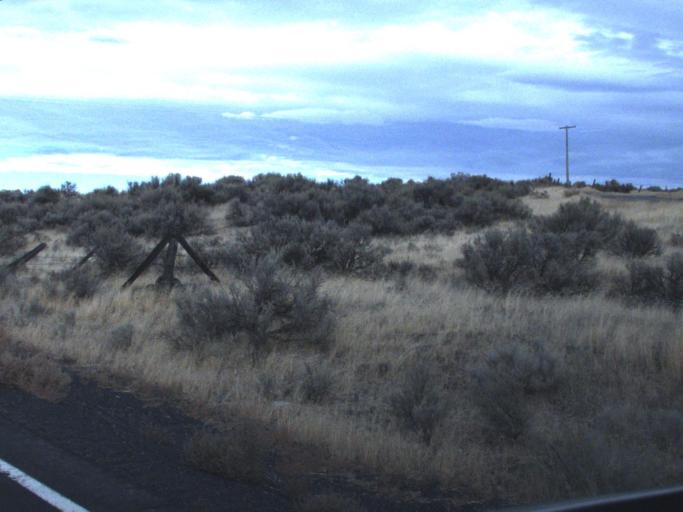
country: US
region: Washington
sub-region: Adams County
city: Ritzville
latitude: 47.4243
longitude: -118.7021
